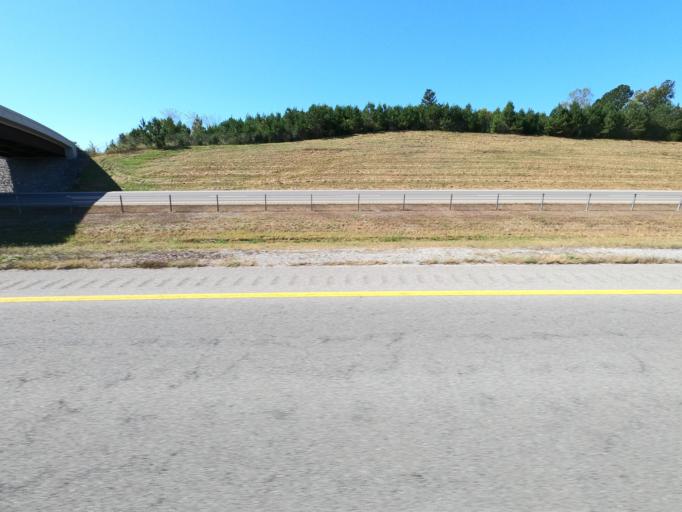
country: US
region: Tennessee
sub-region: Williamson County
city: Fairview
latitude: 35.8641
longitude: -87.0877
